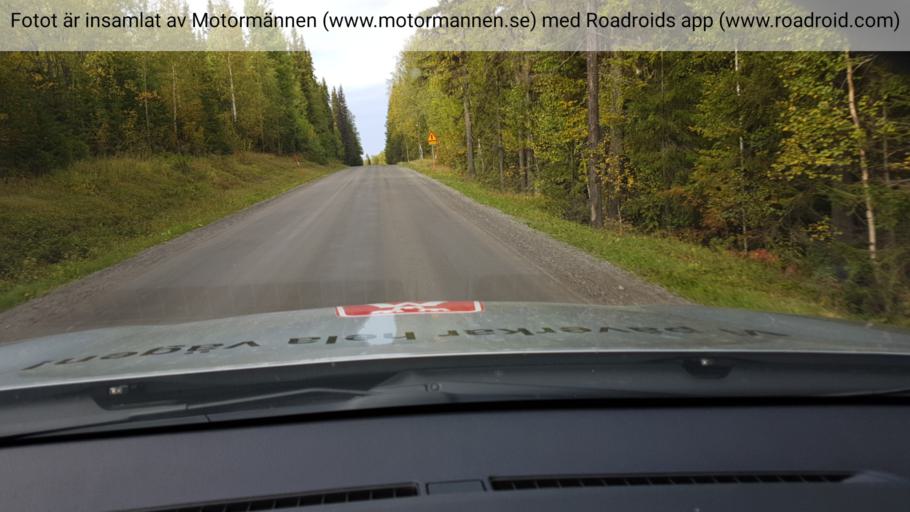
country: SE
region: Jaemtland
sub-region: Stroemsunds Kommun
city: Stroemsund
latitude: 63.9993
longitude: 15.8166
